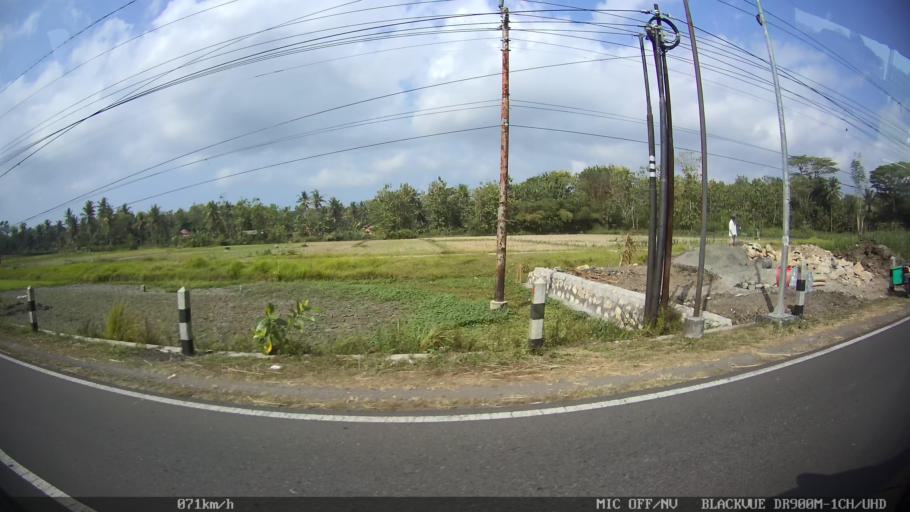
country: ID
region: Daerah Istimewa Yogyakarta
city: Srandakan
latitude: -7.8733
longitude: 110.2001
